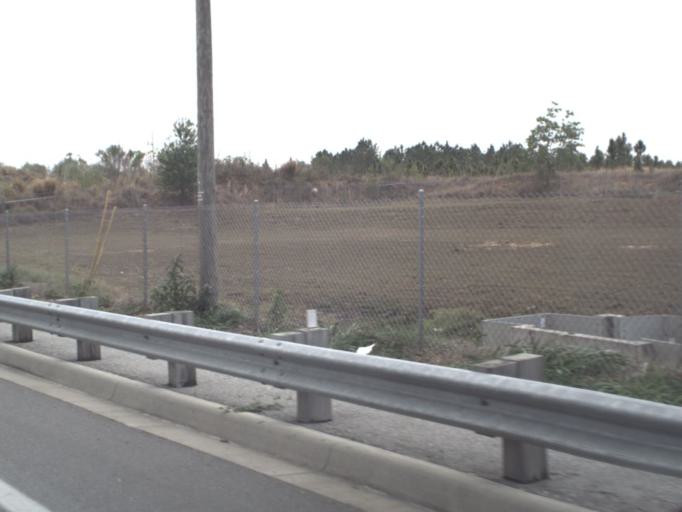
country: US
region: Florida
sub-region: Lake County
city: Minneola
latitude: 28.5465
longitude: -81.7360
